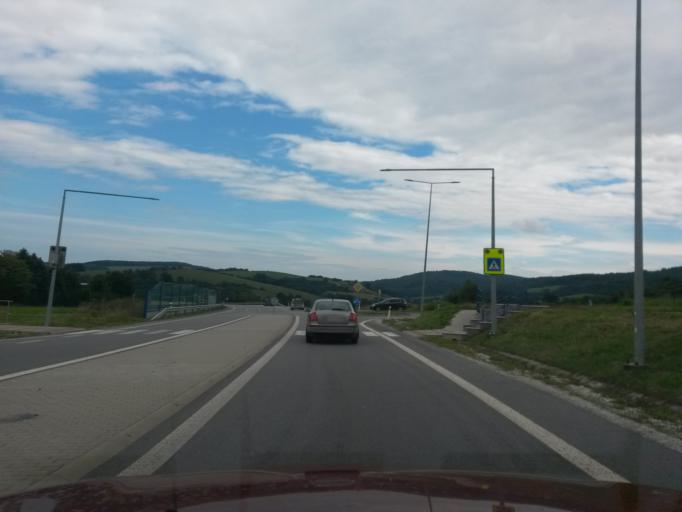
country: SK
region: Presovsky
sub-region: Okres Bardejov
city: Bardejov
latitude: 49.2846
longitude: 21.2637
